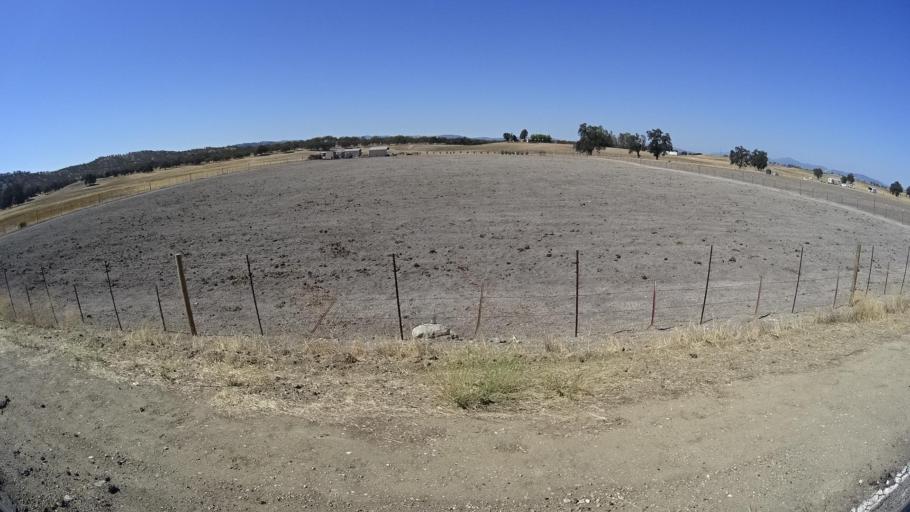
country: US
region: California
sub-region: San Luis Obispo County
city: Lake Nacimiento
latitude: 35.9300
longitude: -121.0817
